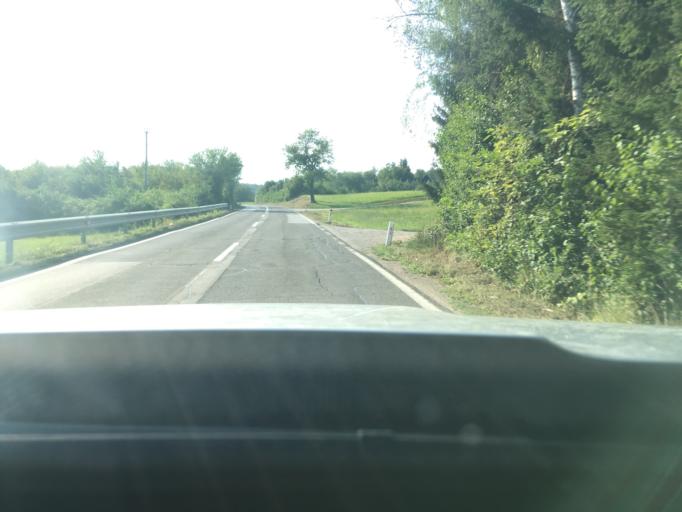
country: SI
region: Metlika
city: Metlika
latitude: 45.6538
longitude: 15.2997
